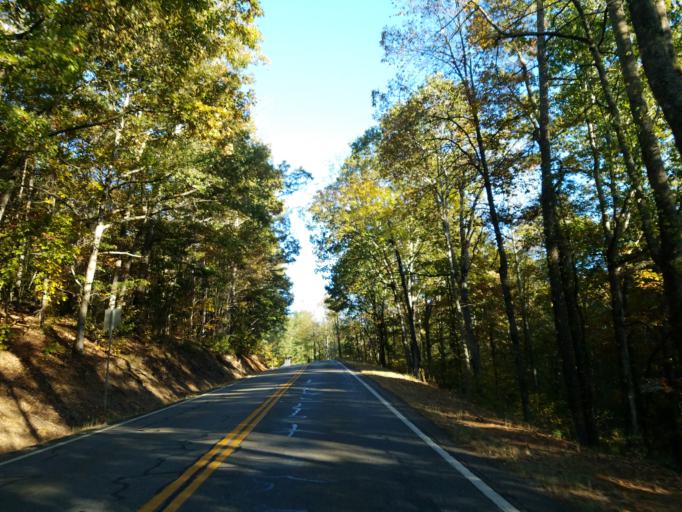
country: US
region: Georgia
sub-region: Pickens County
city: Nelson
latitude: 34.4157
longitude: -84.2615
